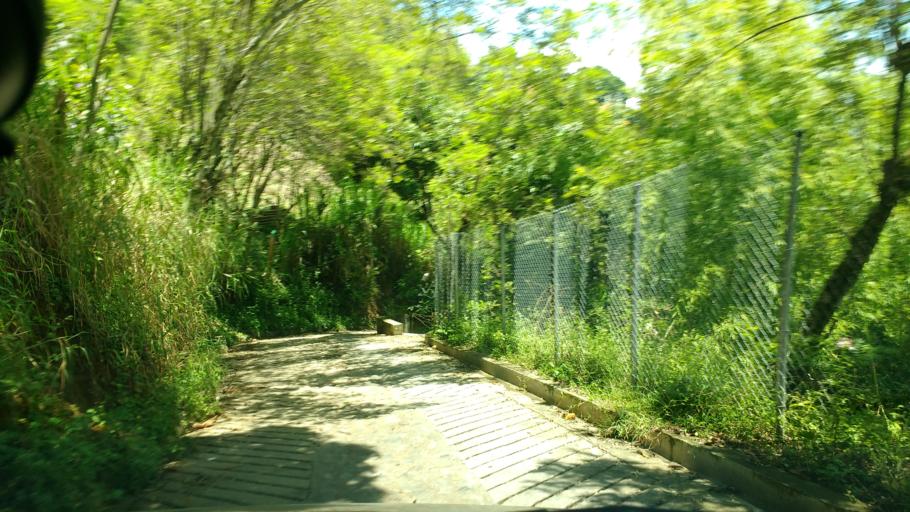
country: CO
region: Antioquia
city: Santa Barbara
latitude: 5.8576
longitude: -75.5576
